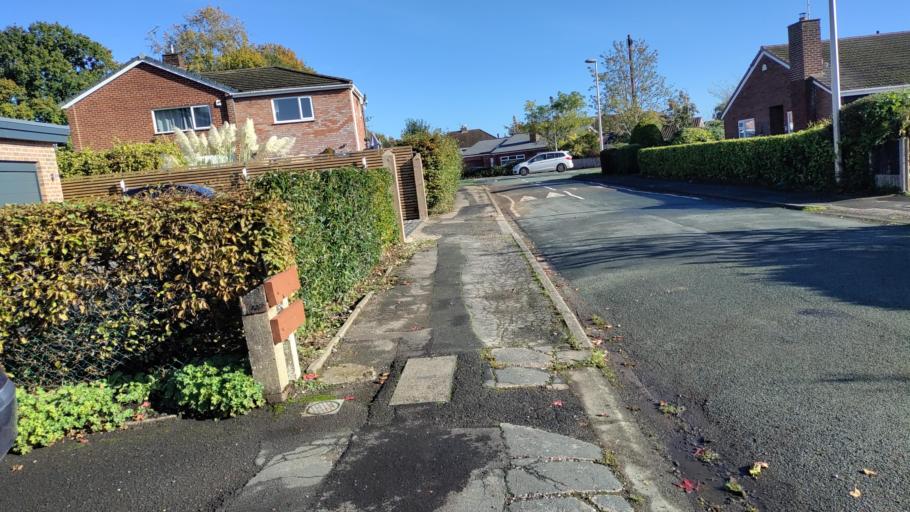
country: GB
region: England
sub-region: Cheshire West and Chester
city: Hartford
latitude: 53.2431
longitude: -2.5455
